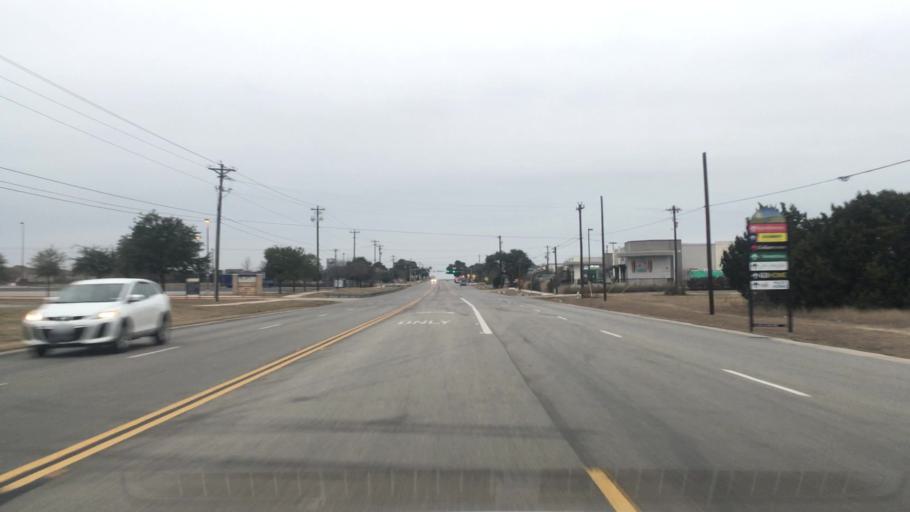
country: US
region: Texas
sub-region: Williamson County
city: Leander
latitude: 30.5372
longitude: -97.8480
